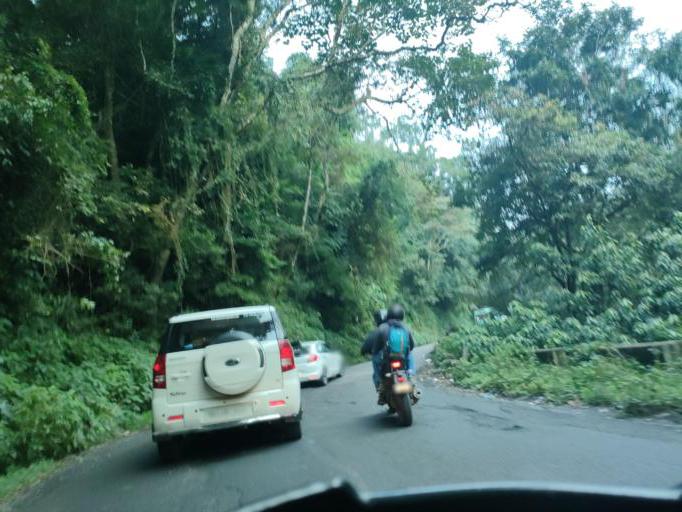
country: IN
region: Tamil Nadu
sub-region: Dindigul
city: Kodaikanal
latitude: 10.2510
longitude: 77.5219
